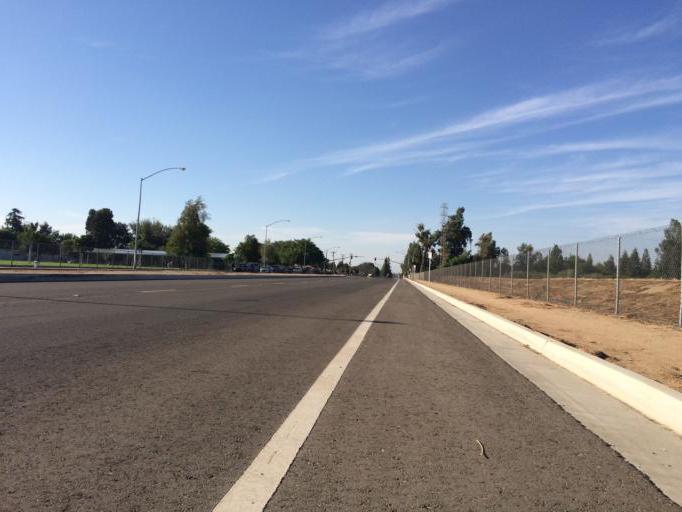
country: US
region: California
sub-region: Fresno County
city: Sunnyside
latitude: 36.7416
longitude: -119.6819
